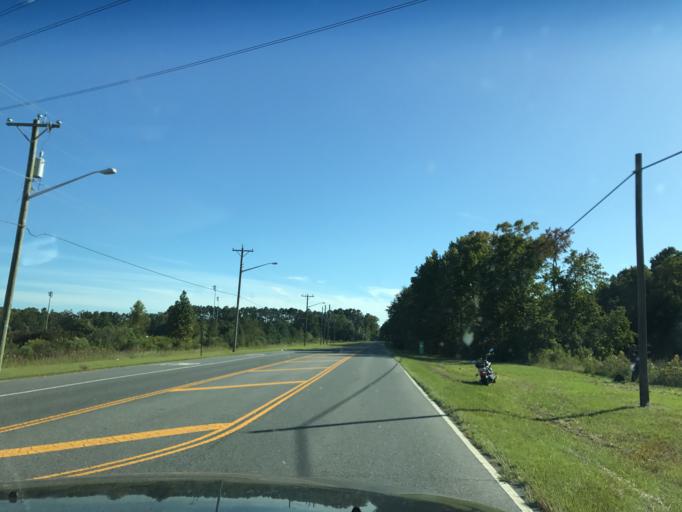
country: US
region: Virginia
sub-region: City of Portsmouth
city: Portsmouth Heights
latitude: 36.7223
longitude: -76.3499
